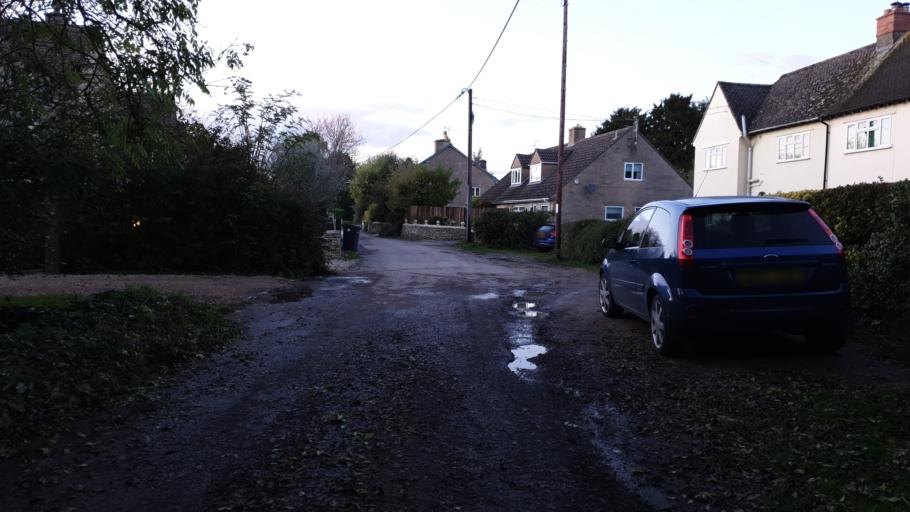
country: GB
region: England
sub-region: Wiltshire
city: Minety
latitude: 51.6513
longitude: -1.9715
